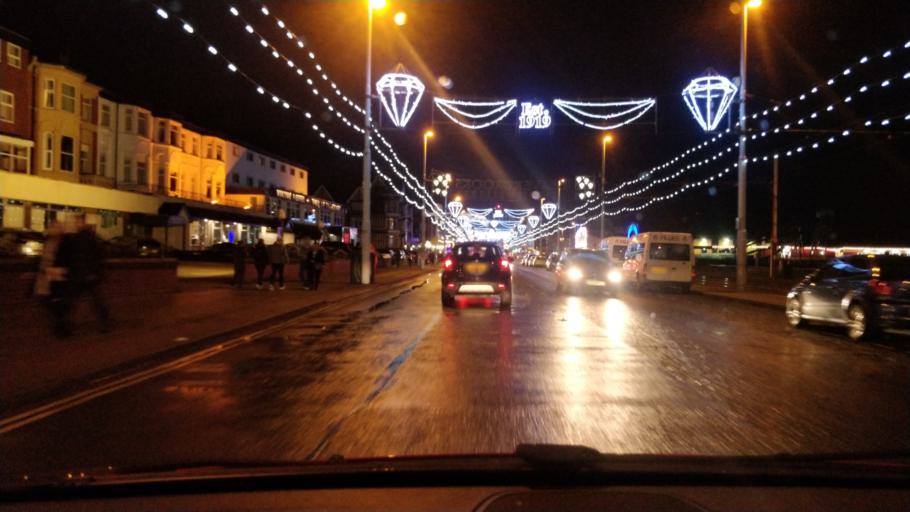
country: GB
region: England
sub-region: Blackpool
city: Blackpool
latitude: 53.7969
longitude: -3.0560
